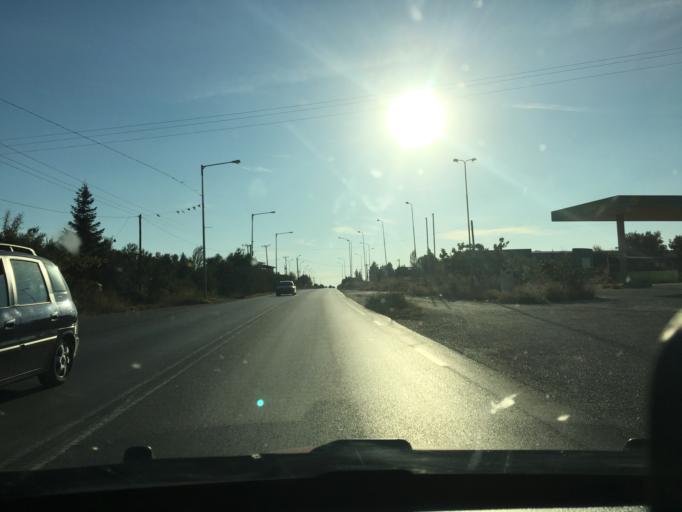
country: GR
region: Central Macedonia
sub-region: Nomos Chalkidikis
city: Olynthos
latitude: 40.2558
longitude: 23.3239
